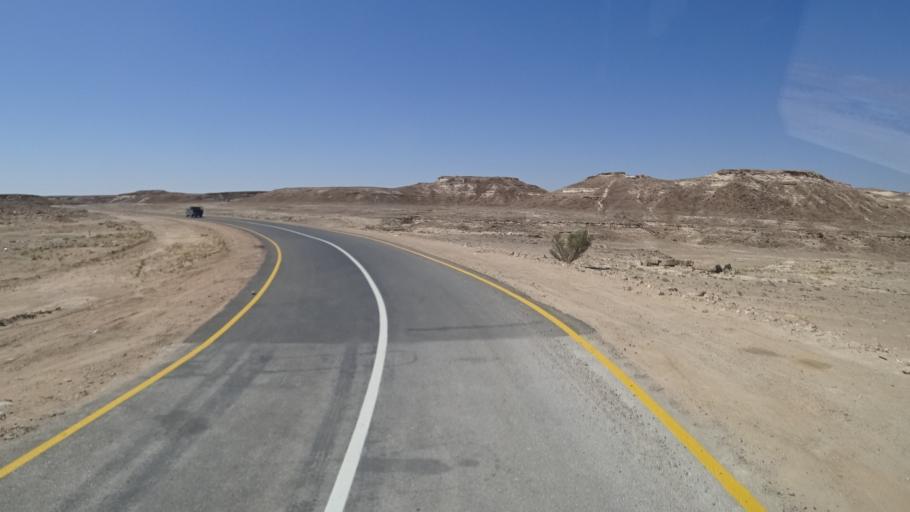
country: OM
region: Zufar
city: Salalah
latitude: 17.4762
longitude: 53.3512
